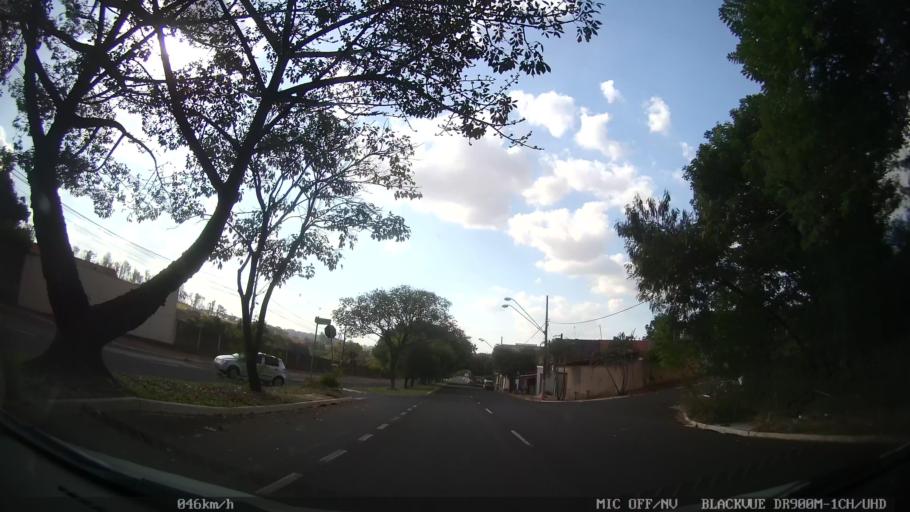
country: BR
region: Sao Paulo
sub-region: Ribeirao Preto
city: Ribeirao Preto
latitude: -21.1908
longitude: -47.8446
